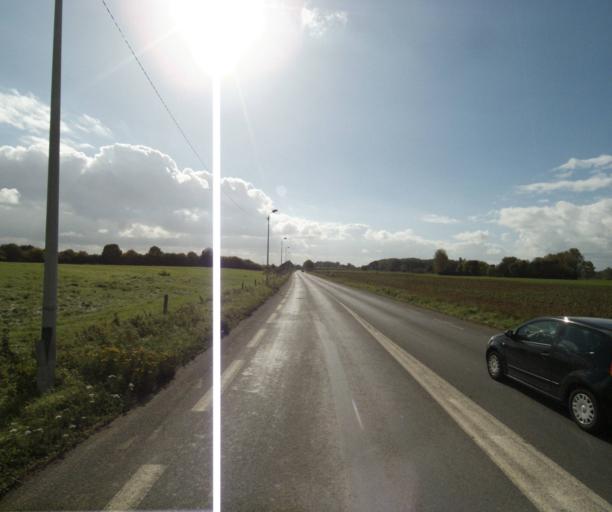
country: FR
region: Nord-Pas-de-Calais
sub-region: Departement du Nord
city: Deulemont
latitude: 50.7266
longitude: 2.9407
